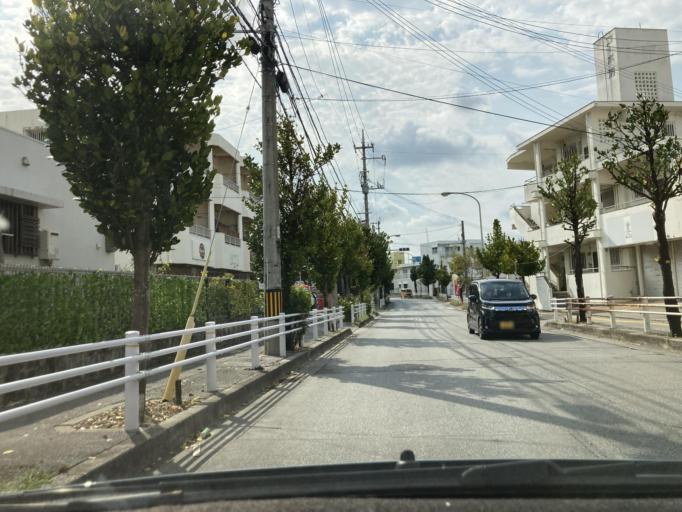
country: JP
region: Okinawa
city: Tomigusuku
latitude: 26.2002
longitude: 127.7175
